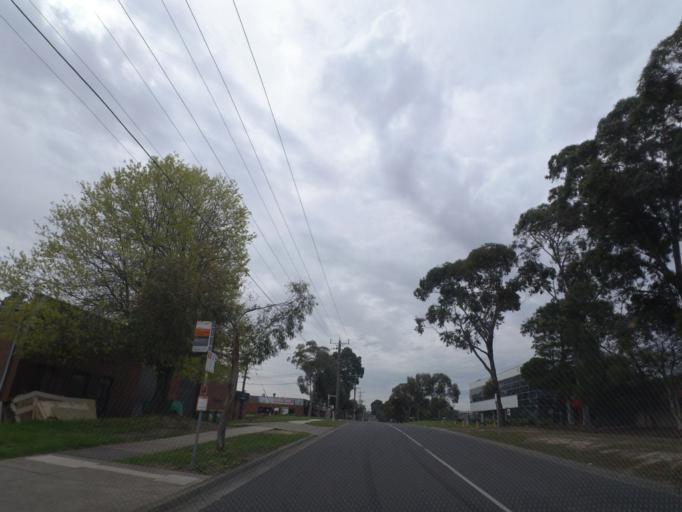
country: AU
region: Victoria
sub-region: Knox
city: Bayswater
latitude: -37.8445
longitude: 145.2789
